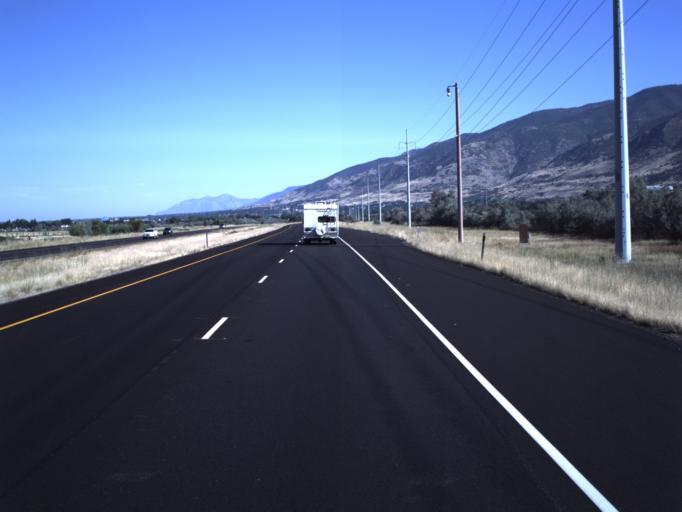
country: US
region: Utah
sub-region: Davis County
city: Centerville
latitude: 40.9453
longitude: -111.8925
